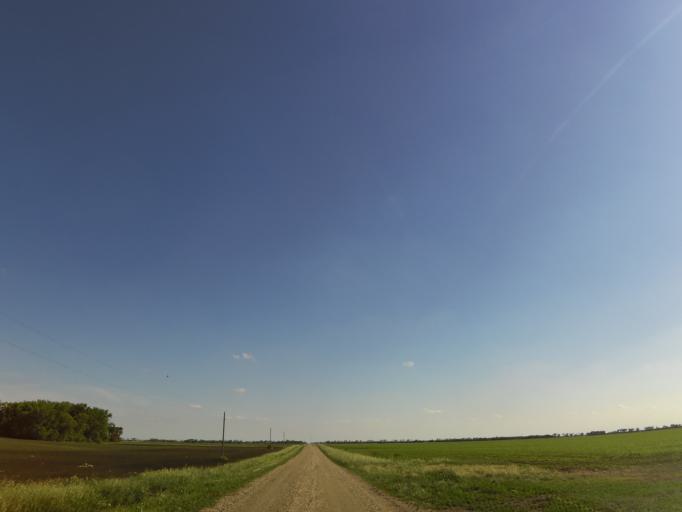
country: US
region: North Dakota
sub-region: Walsh County
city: Grafton
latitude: 48.3463
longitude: -97.2329
